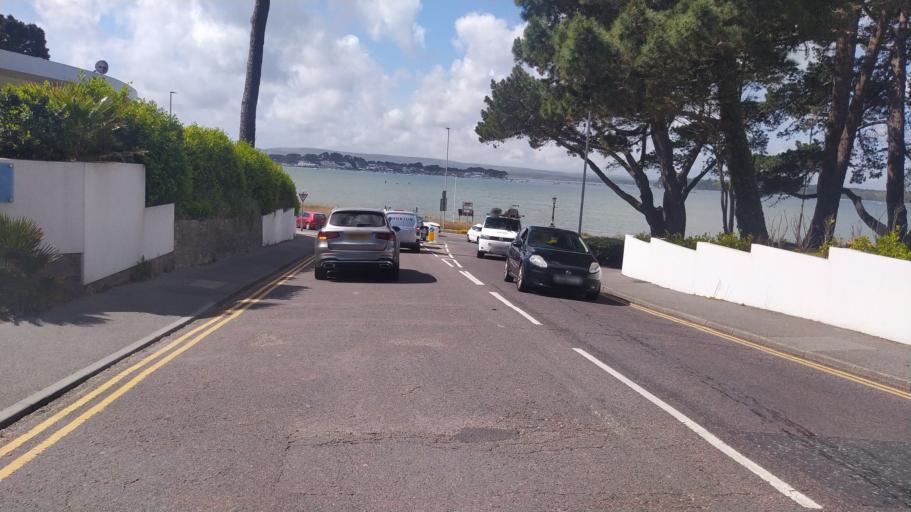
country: GB
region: England
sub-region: Dorset
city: Parkstone
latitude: 50.6988
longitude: -1.9325
